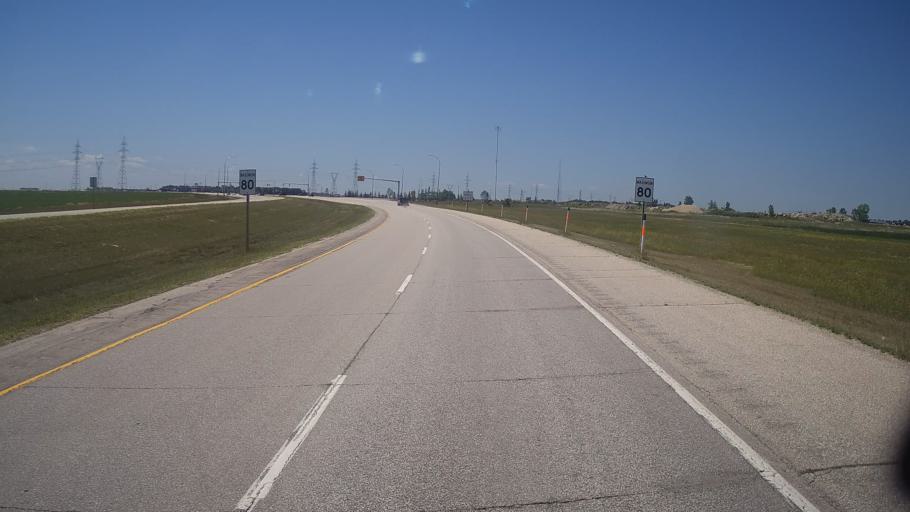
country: CA
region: Manitoba
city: Stonewall
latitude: 49.9893
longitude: -97.3046
